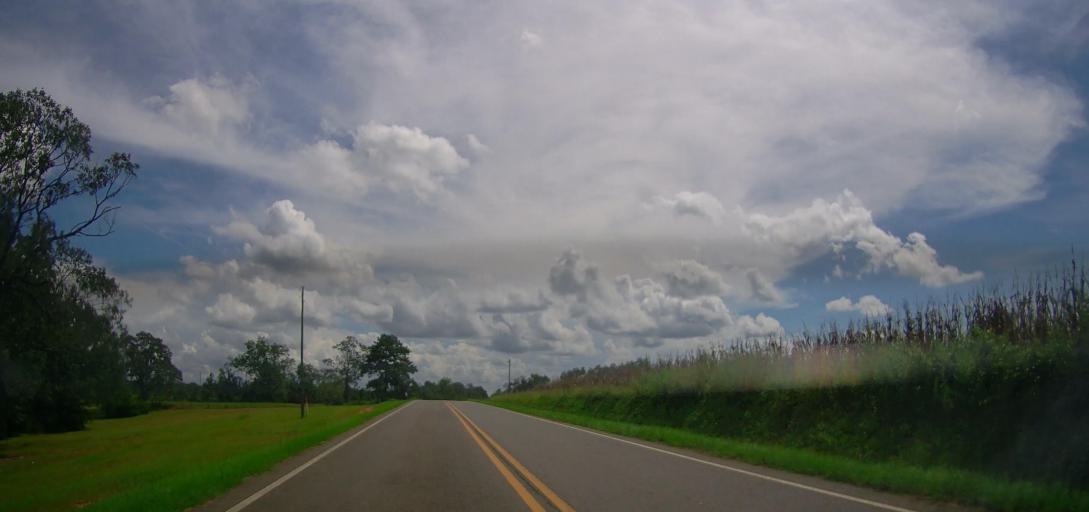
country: US
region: Georgia
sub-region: Taylor County
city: Butler
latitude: 32.5214
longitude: -84.2056
